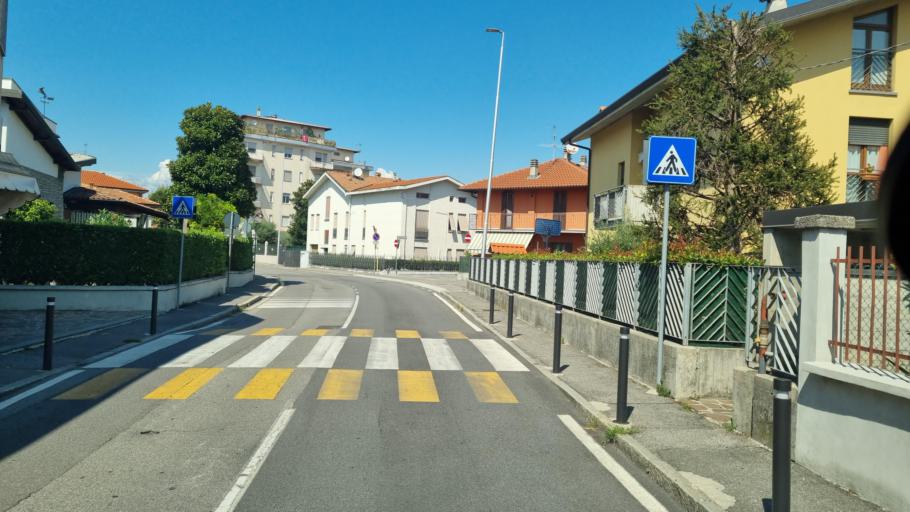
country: IT
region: Lombardy
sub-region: Provincia di Bergamo
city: Azzano San Paolo
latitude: 45.6635
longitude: 9.6722
